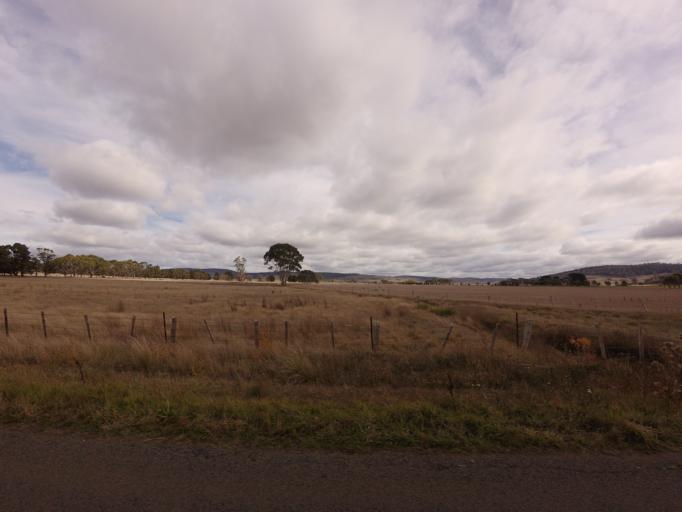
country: AU
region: Tasmania
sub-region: Brighton
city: Bridgewater
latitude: -42.4074
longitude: 147.3962
